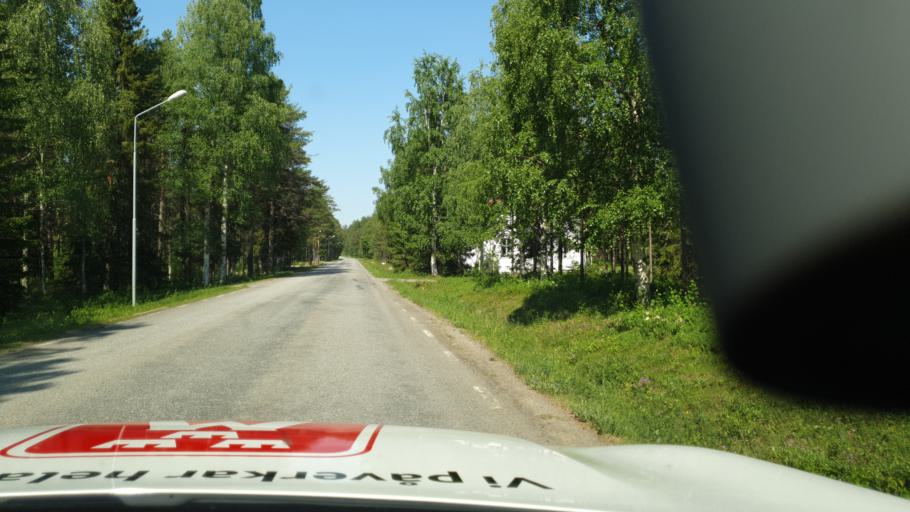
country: SE
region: Vaesterbotten
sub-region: Skelleftea Kommun
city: Langsele
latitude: 64.9544
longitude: 19.9170
